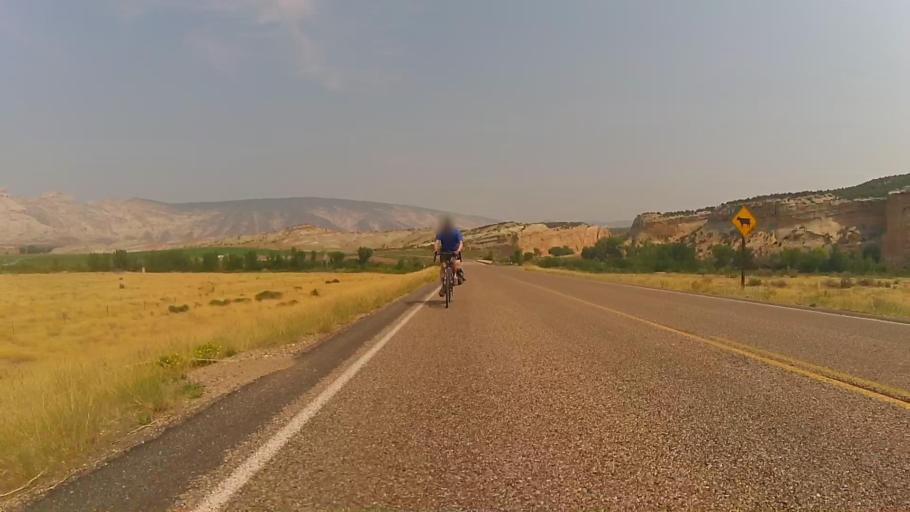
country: US
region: Utah
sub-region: Uintah County
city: Naples
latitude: 40.4083
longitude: -109.2364
